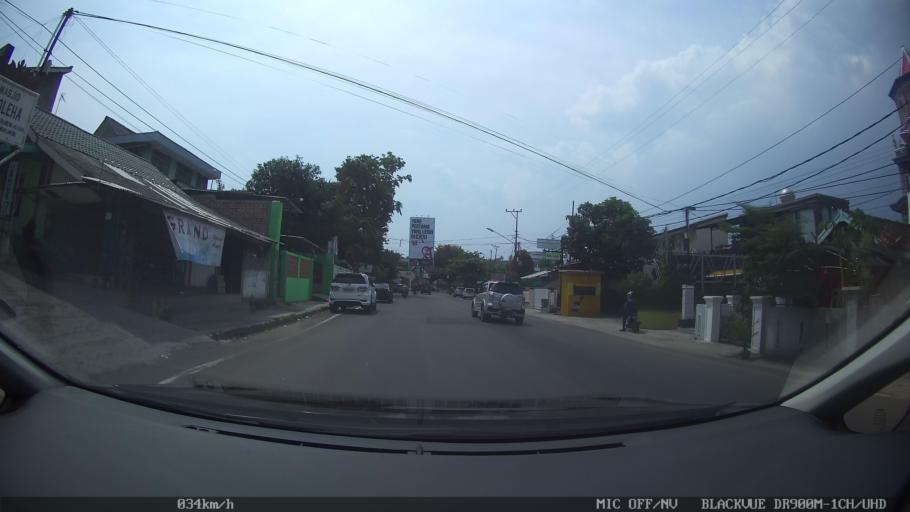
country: ID
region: Lampung
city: Bandarlampung
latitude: -5.4422
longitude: 105.2656
